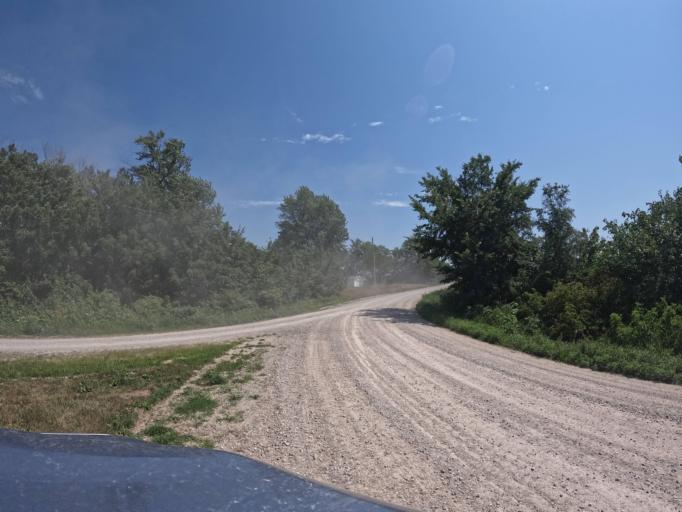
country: US
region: Iowa
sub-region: Henry County
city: Mount Pleasant
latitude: 40.9131
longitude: -91.6366
